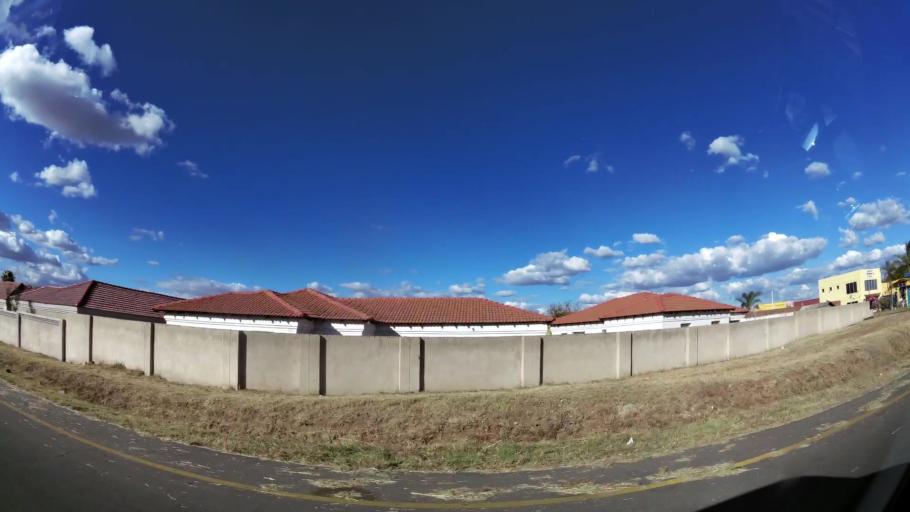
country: ZA
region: Limpopo
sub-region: Capricorn District Municipality
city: Polokwane
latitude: -23.9353
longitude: 29.4494
